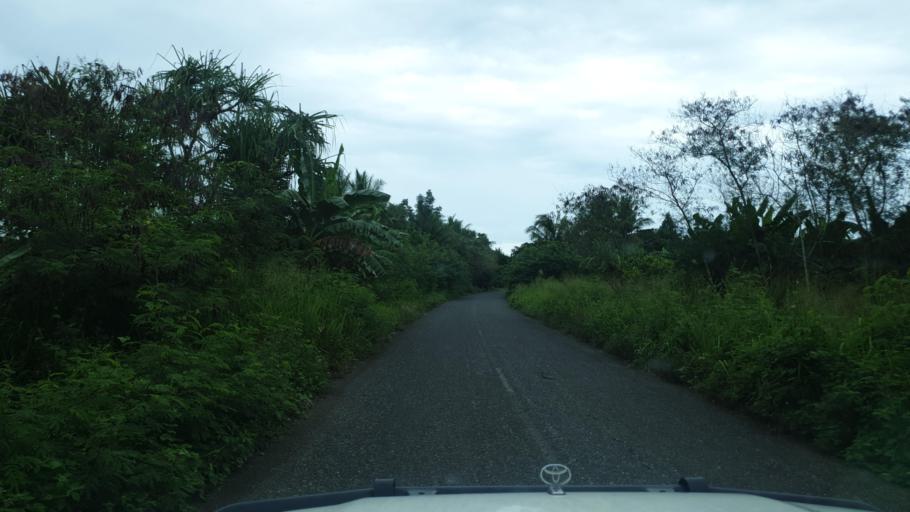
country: PG
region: Gulf
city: Kerema
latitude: -8.1937
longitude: 146.2131
